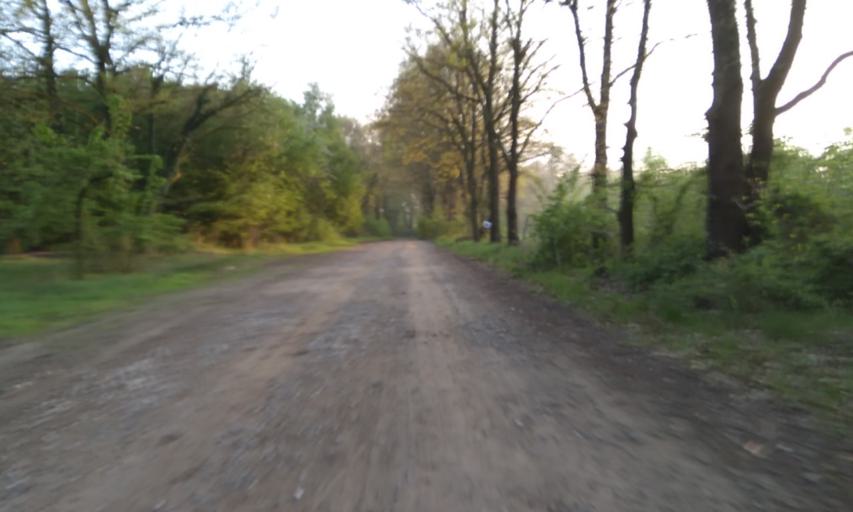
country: DE
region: Lower Saxony
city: Bargstedt
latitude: 53.4979
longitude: 9.4383
